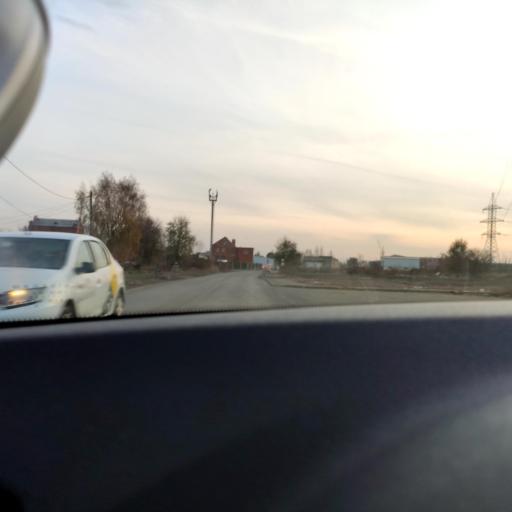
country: RU
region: Samara
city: Petra-Dubrava
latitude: 53.2563
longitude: 50.3121
